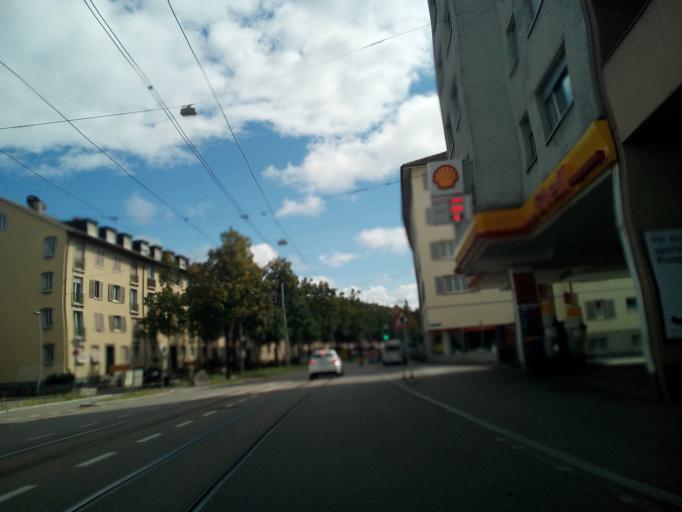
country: FR
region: Alsace
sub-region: Departement du Haut-Rhin
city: Village-Neuf
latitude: 47.5854
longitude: 7.5933
